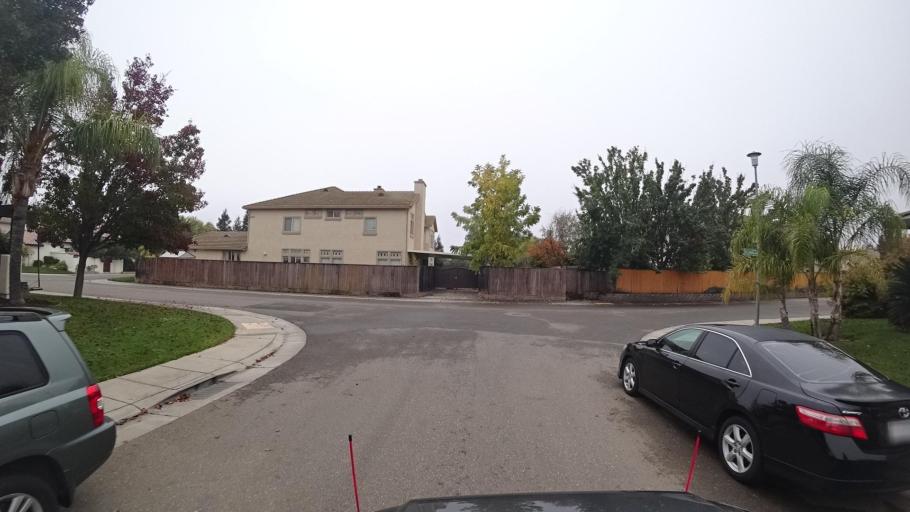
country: US
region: California
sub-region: Sacramento County
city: Elk Grove
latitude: 38.4081
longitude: -121.3407
